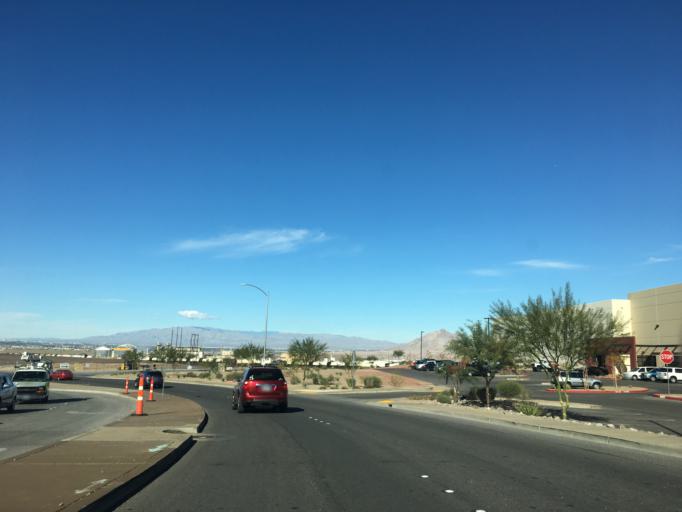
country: US
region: Nevada
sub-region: Clark County
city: Henderson
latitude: 36.0349
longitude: -115.0079
